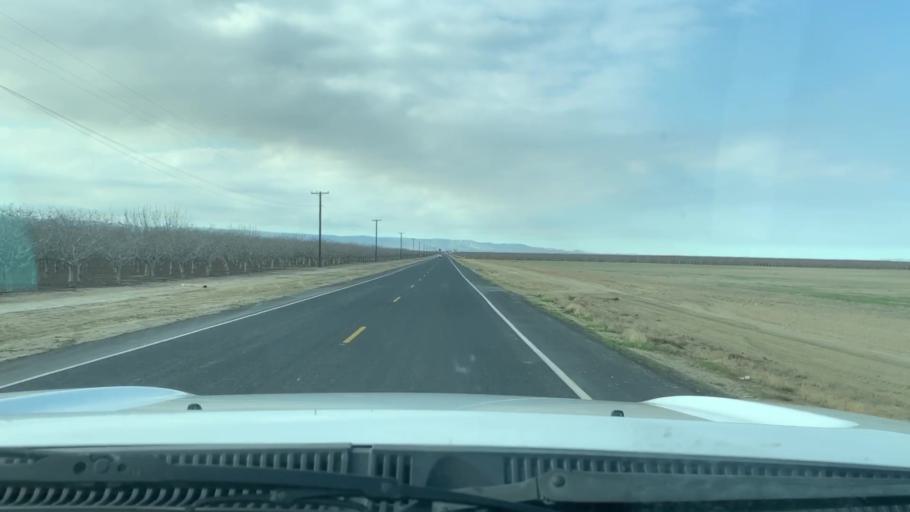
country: US
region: California
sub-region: Kern County
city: Lost Hills
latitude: 35.4994
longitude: -119.6225
